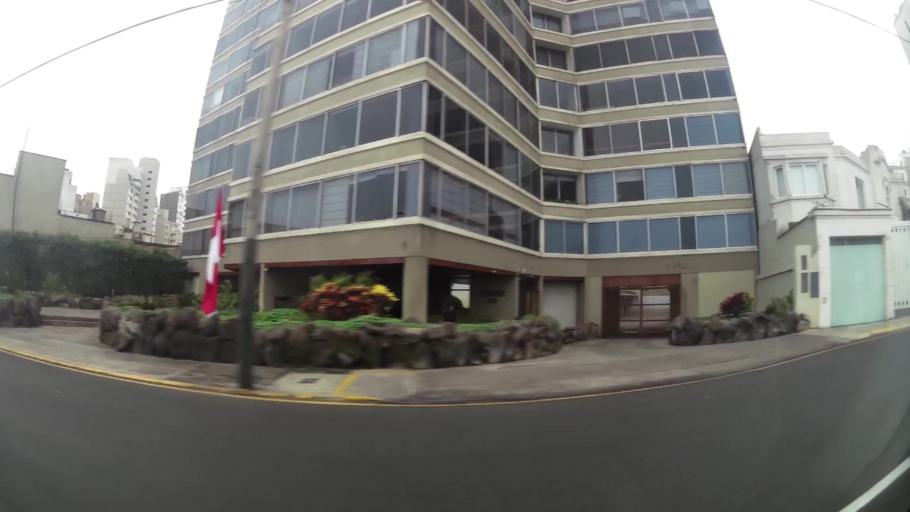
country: PE
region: Lima
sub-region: Lima
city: San Isidro
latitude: -12.1302
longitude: -77.0332
